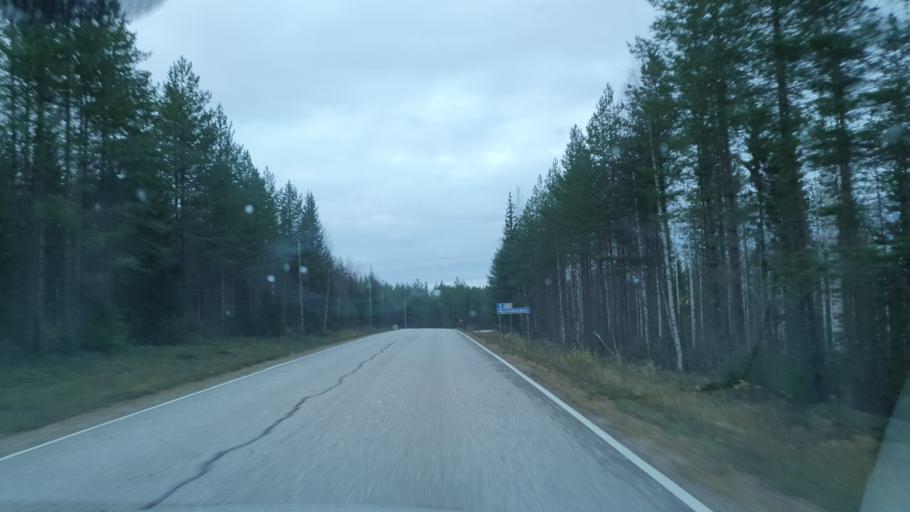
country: FI
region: Kainuu
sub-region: Kajaani
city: Ristijaervi
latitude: 64.4344
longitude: 28.3683
